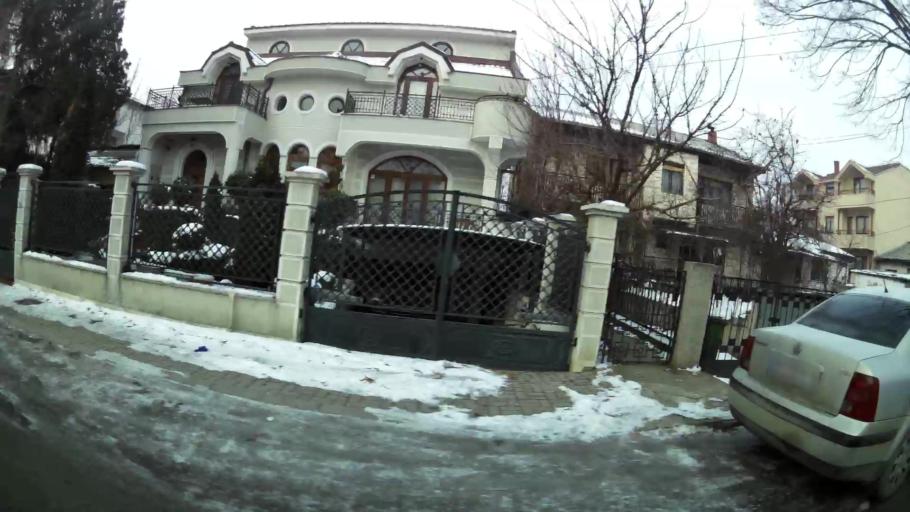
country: MK
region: Butel
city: Butel
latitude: 42.0228
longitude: 21.4482
